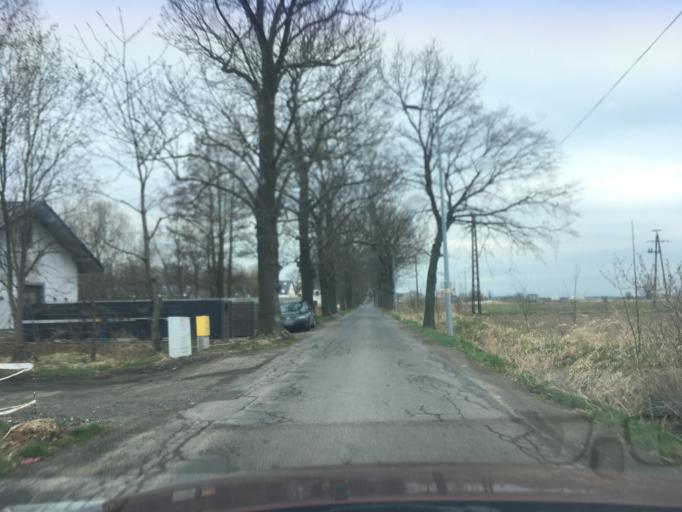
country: PL
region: Lower Silesian Voivodeship
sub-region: Powiat zgorzelecki
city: Lagow
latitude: 51.1682
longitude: 15.0360
